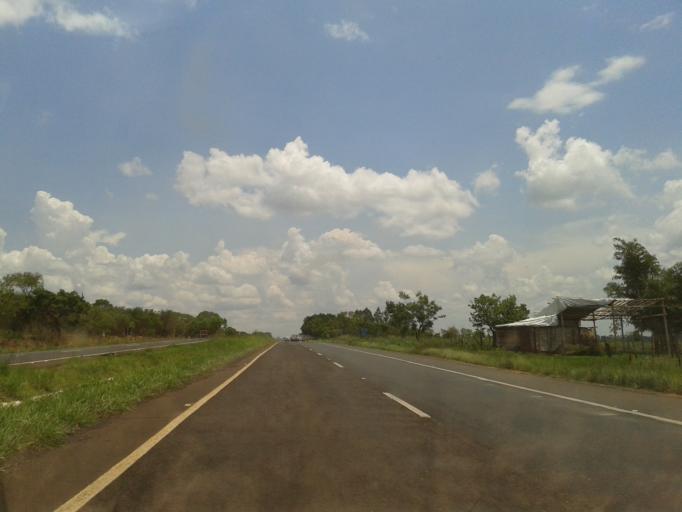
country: BR
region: Minas Gerais
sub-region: Monte Alegre De Minas
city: Monte Alegre de Minas
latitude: -18.8765
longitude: -48.9056
